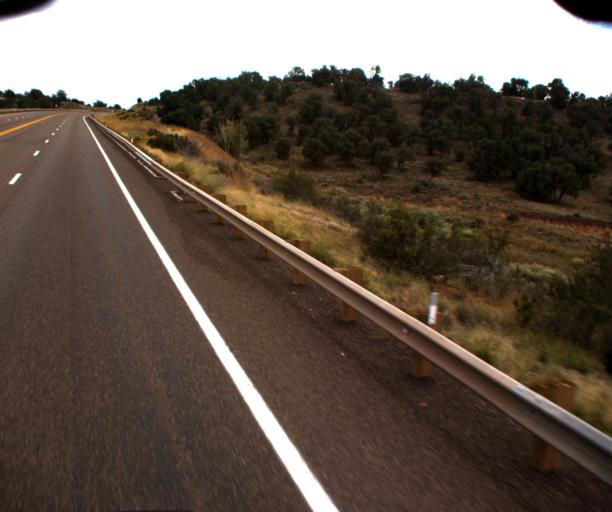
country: US
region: Arizona
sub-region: Navajo County
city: White Mountain Lake
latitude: 34.3764
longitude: -110.0543
